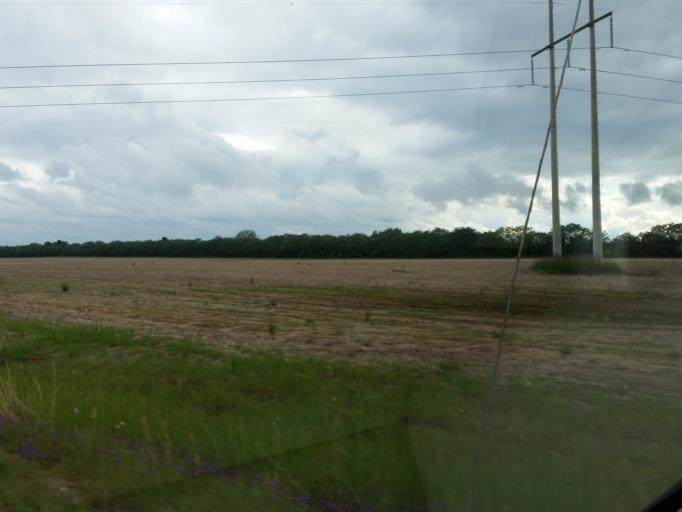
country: US
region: Georgia
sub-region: Peach County
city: Byron
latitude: 32.6634
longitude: -83.8065
